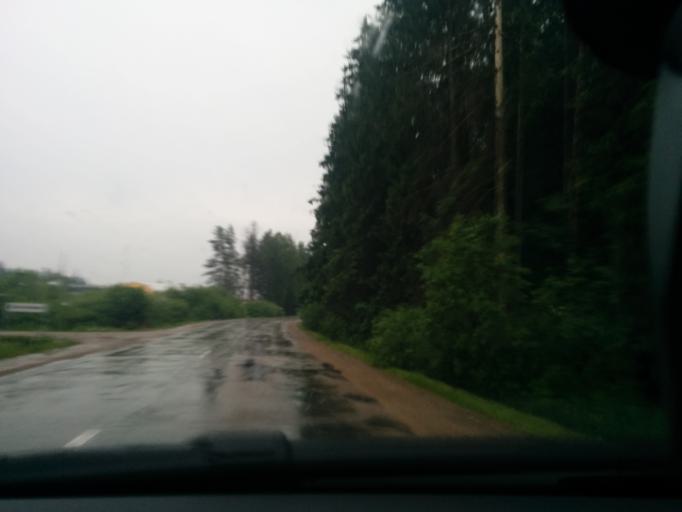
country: LV
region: Ogre
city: Ogre
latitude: 56.8273
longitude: 24.5963
